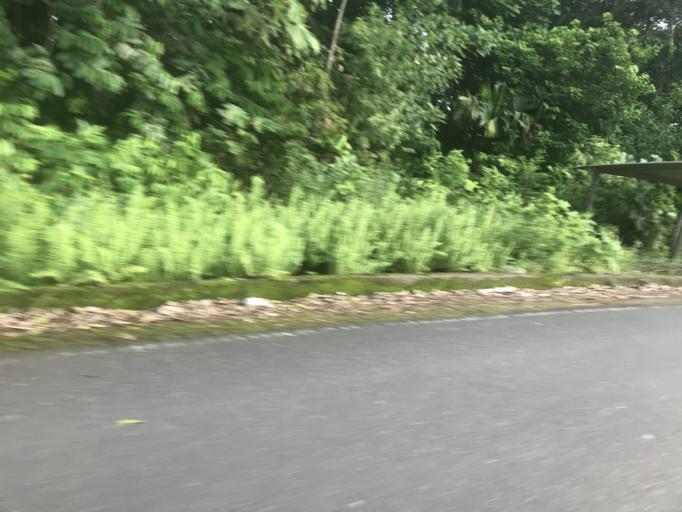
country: EC
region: Napo
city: Tena
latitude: -1.0443
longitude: -77.8083
